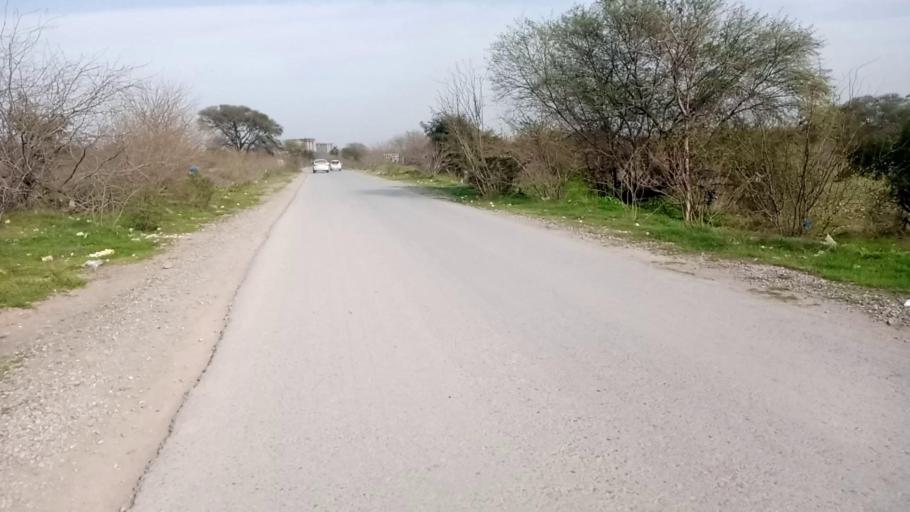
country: PK
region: Khyber Pakhtunkhwa
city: Peshawar
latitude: 34.0057
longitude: 71.4498
